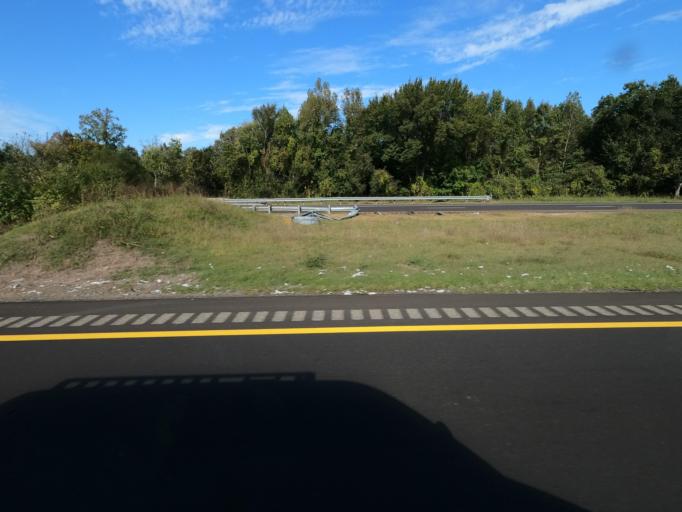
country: US
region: Tennessee
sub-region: Fayette County
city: Hickory Withe
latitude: 35.3108
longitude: -89.5839
